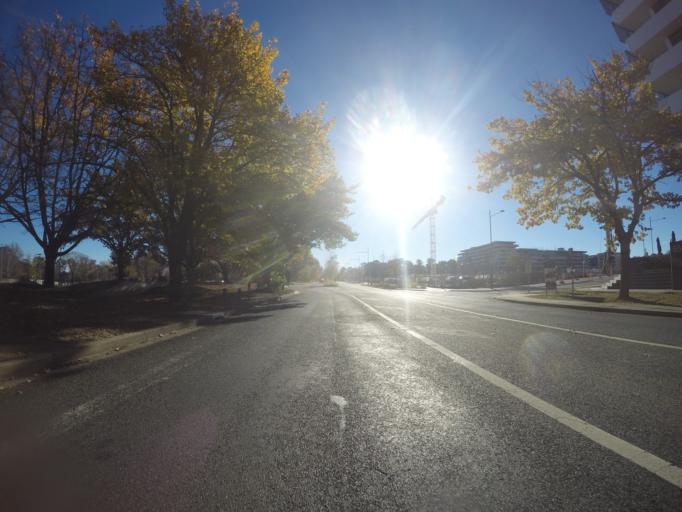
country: AU
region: Australian Capital Territory
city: Canberra
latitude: -35.2912
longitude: 149.1444
